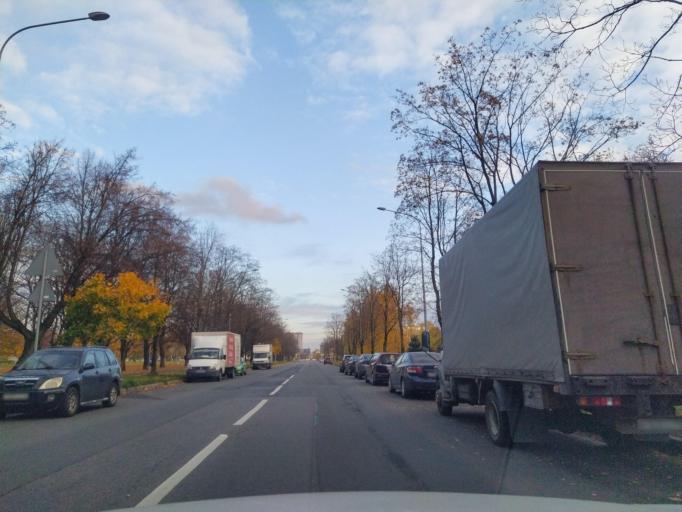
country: RU
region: Leningrad
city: Kalininskiy
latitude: 59.9819
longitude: 30.4137
